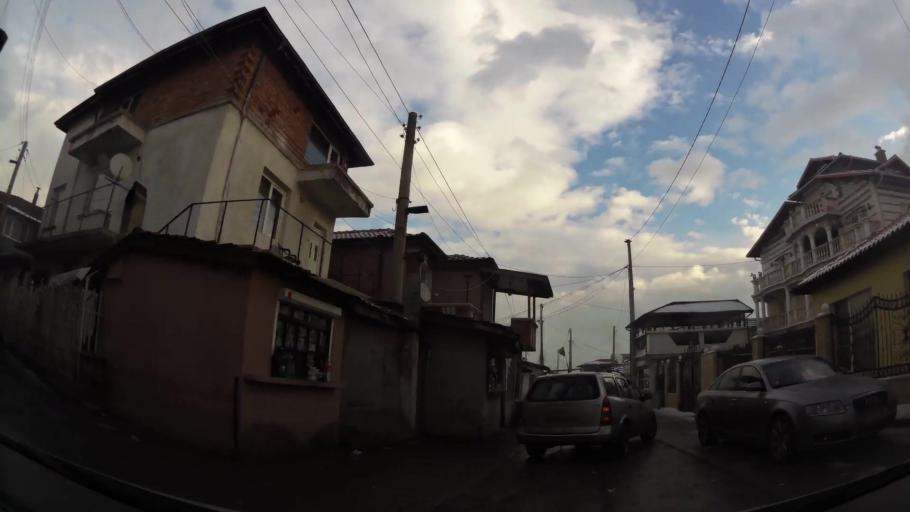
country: BG
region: Sofia-Capital
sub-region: Stolichna Obshtina
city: Sofia
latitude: 42.6938
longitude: 23.2645
